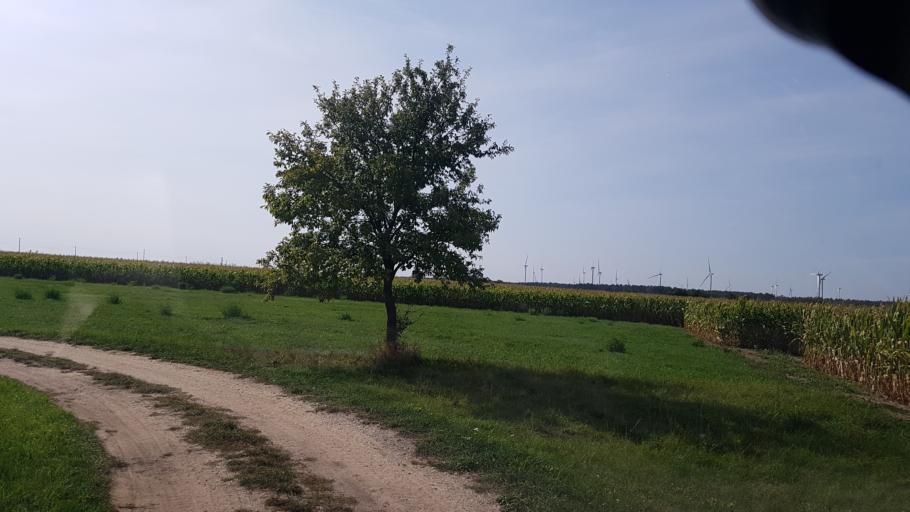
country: DE
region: Brandenburg
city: Trobitz
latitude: 51.6635
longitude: 13.4260
